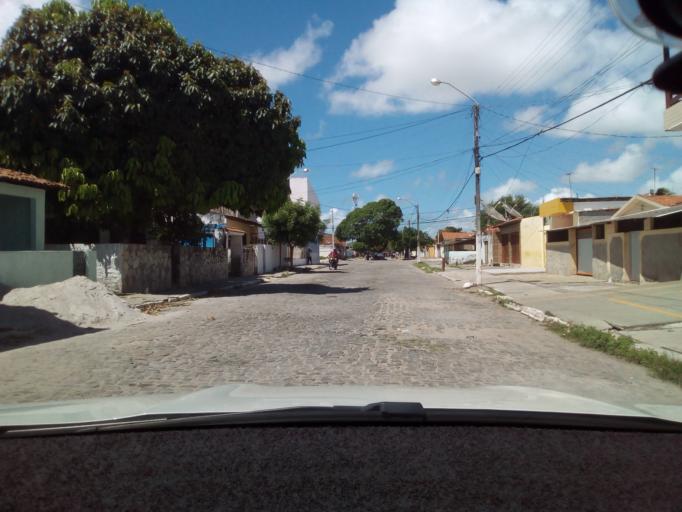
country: BR
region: Paraiba
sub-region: Cabedelo
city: Cabedelo
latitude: -6.9805
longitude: -34.8336
